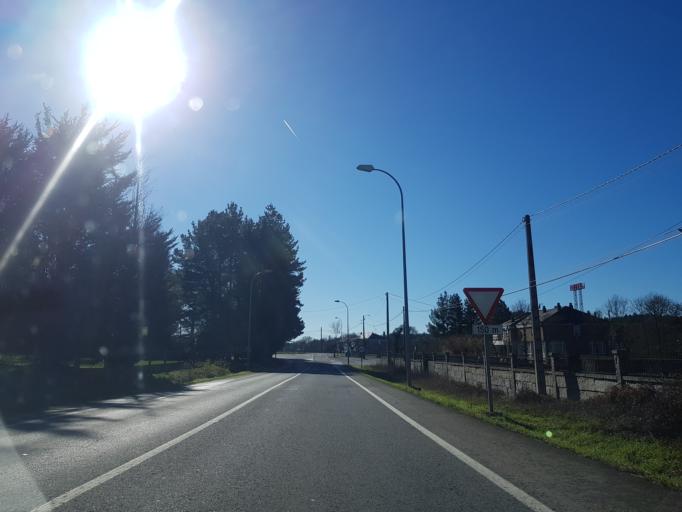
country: ES
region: Galicia
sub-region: Provincia de Lugo
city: Guitiriz
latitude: 43.1803
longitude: -7.8277
